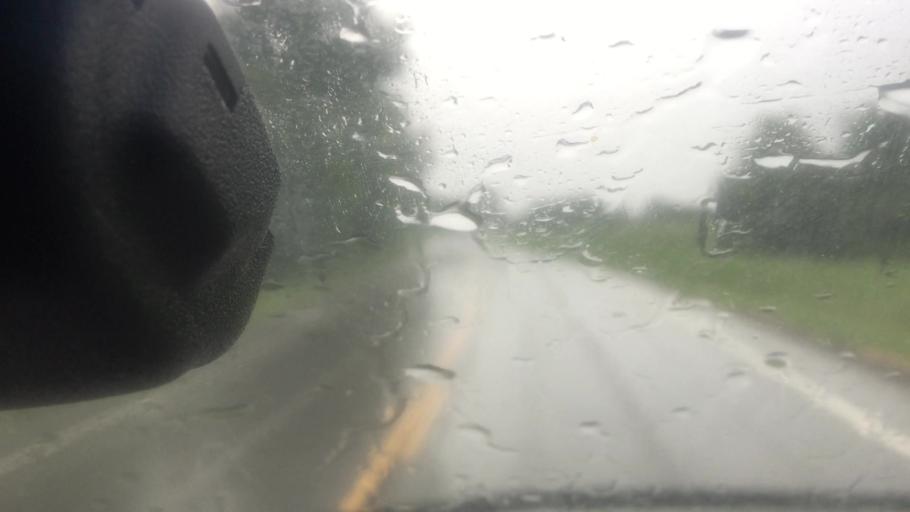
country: US
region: Illinois
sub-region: Madison County
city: Edwardsville
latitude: 38.8318
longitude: -89.9205
